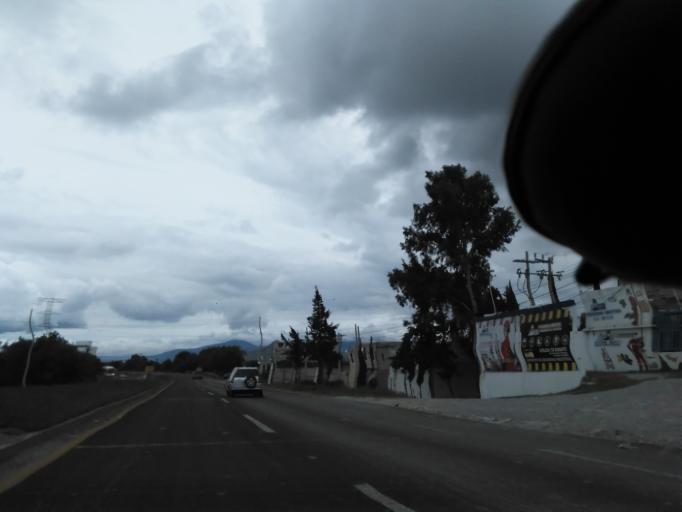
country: MX
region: Hidalgo
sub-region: Atitalaquia
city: Unidad Habitacional Antonio Osorio de Leon (Bojay)
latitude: 20.0586
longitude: -99.2692
